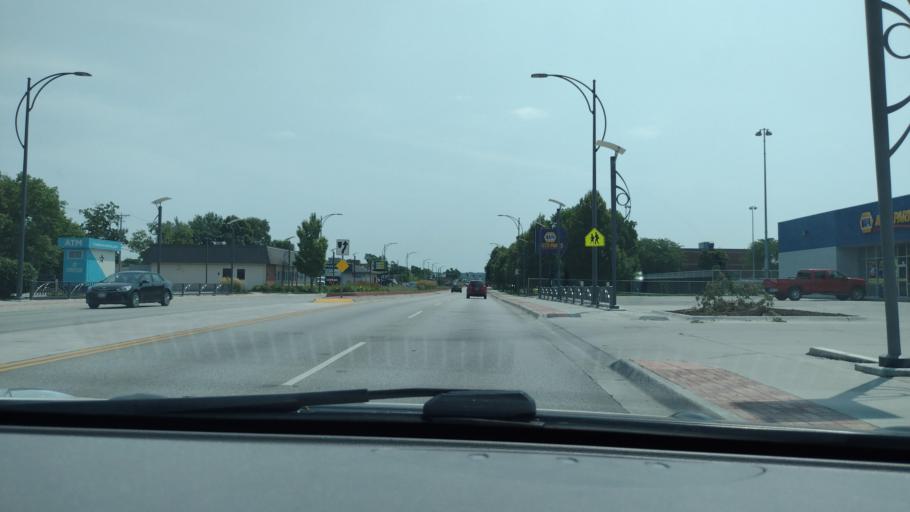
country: US
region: Iowa
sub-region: Pottawattamie County
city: Council Bluffs
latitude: 41.2619
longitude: -95.8863
